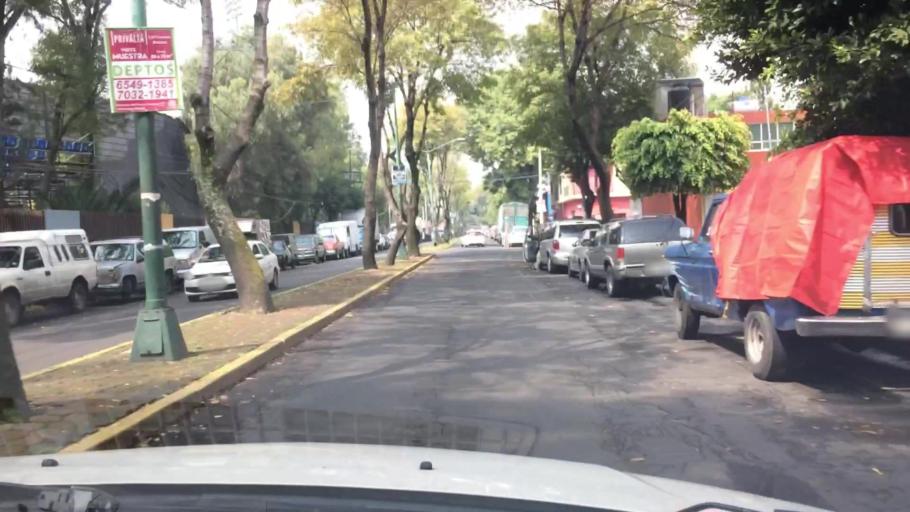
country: MX
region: Mexico City
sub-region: Iztacalco
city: Iztacalco
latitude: 19.4116
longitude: -99.1082
